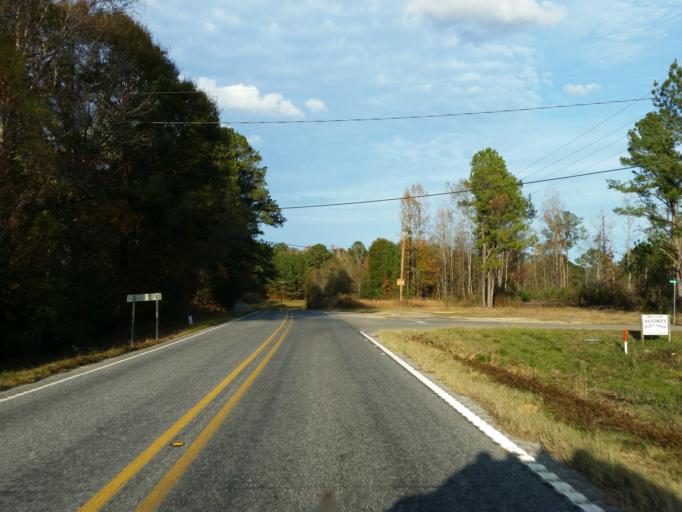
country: US
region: Mississippi
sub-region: Clarke County
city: Stonewall
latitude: 32.2205
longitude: -88.7755
